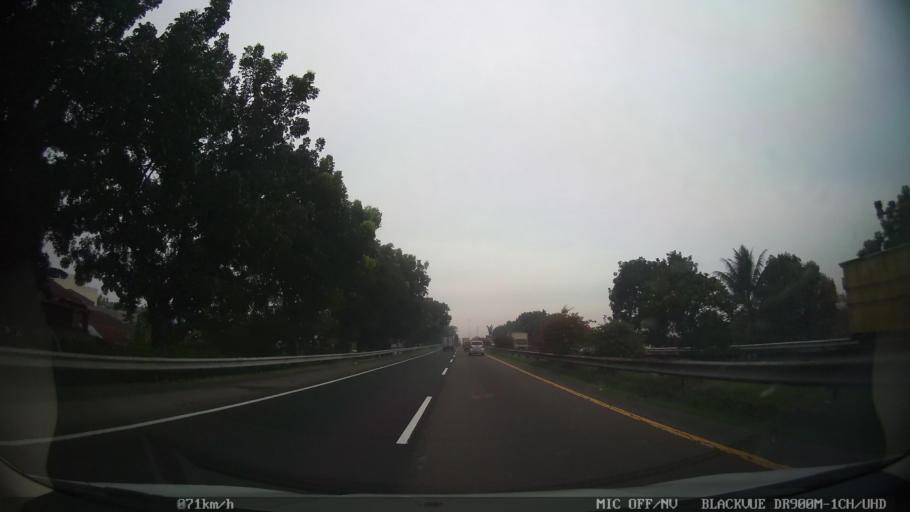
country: ID
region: North Sumatra
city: Medan
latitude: 3.5769
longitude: 98.7250
